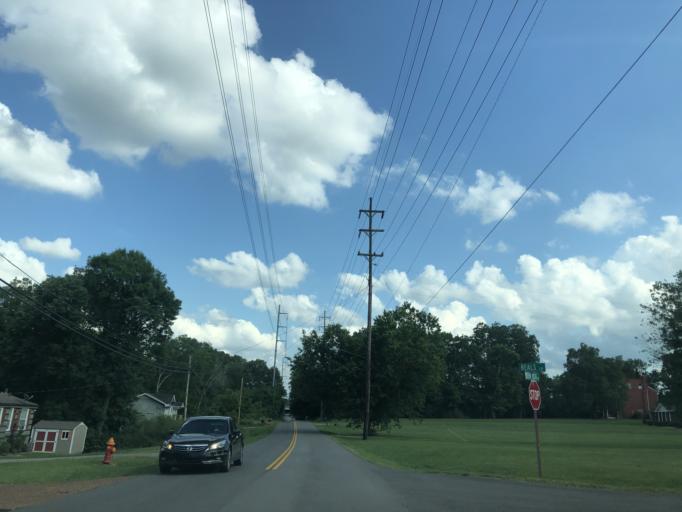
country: US
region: Tennessee
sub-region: Davidson County
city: Nashville
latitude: 36.2357
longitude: -86.8270
